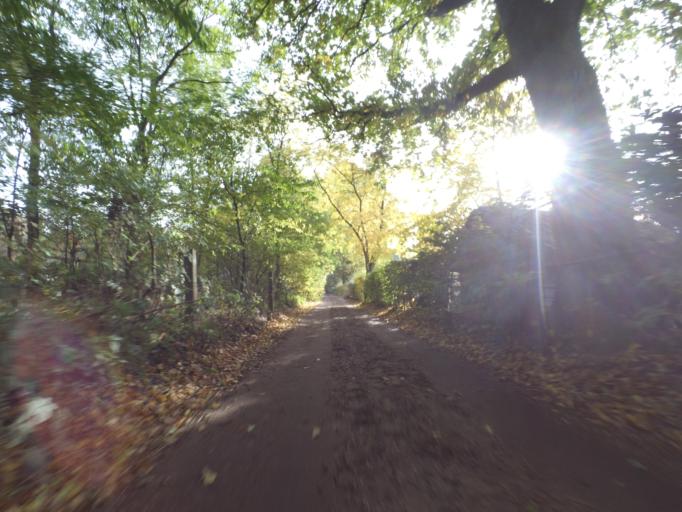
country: NL
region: Gelderland
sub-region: Gemeente Ede
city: Lunteren
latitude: 52.0921
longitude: 5.6315
